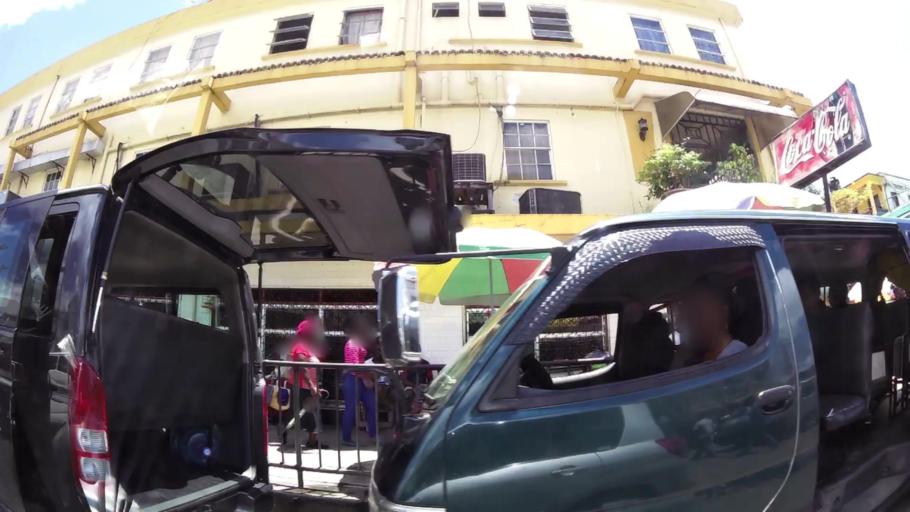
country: GY
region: Demerara-Mahaica
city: Georgetown
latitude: 6.8115
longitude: -58.1665
